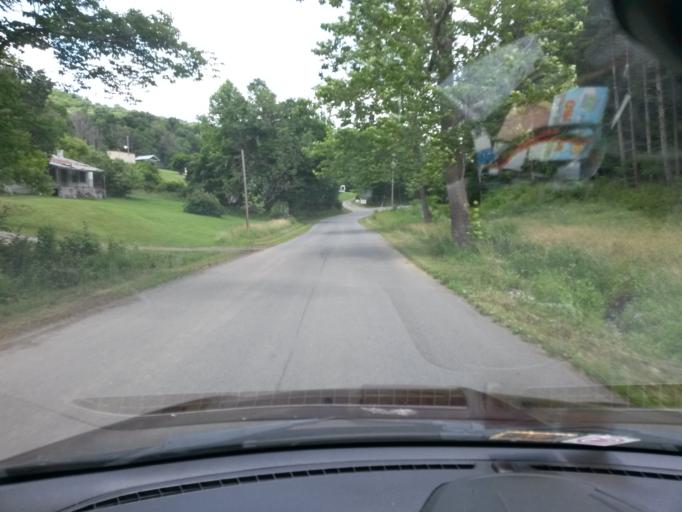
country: US
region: West Virginia
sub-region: Monroe County
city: Union
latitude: 37.5114
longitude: -80.5697
